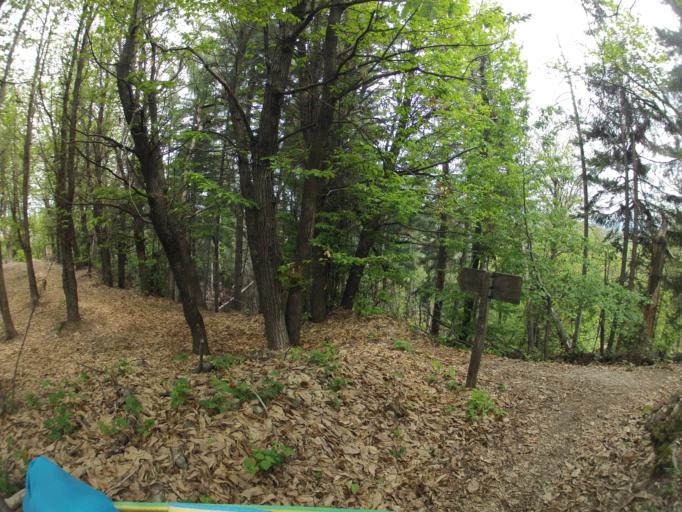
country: IT
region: Piedmont
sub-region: Provincia di Cuneo
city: Peveragno
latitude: 44.3314
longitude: 7.6001
